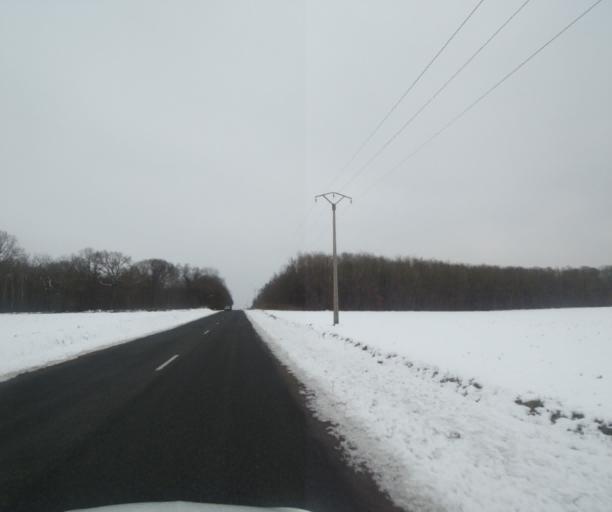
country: FR
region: Champagne-Ardenne
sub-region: Departement de la Haute-Marne
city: Villiers-en-Lieu
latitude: 48.6080
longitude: 4.8831
